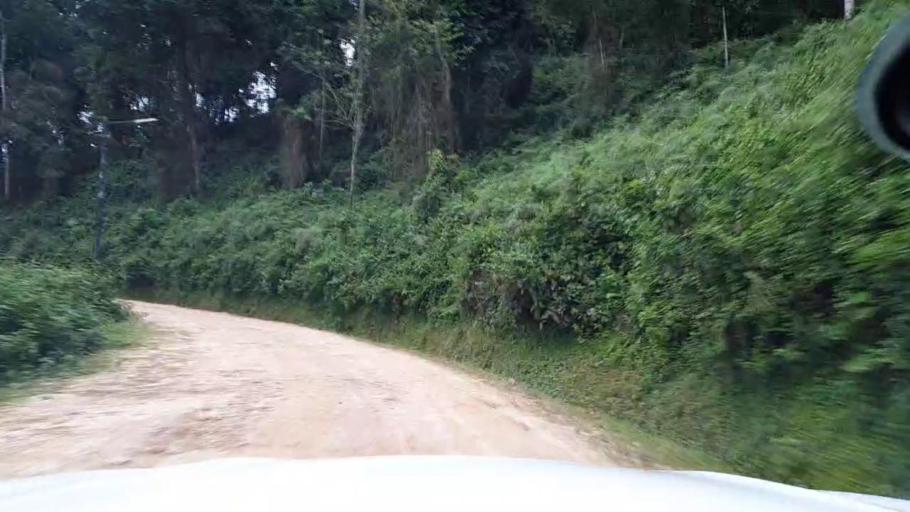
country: RW
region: Western Province
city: Cyangugu
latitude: -2.5643
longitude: 29.2293
